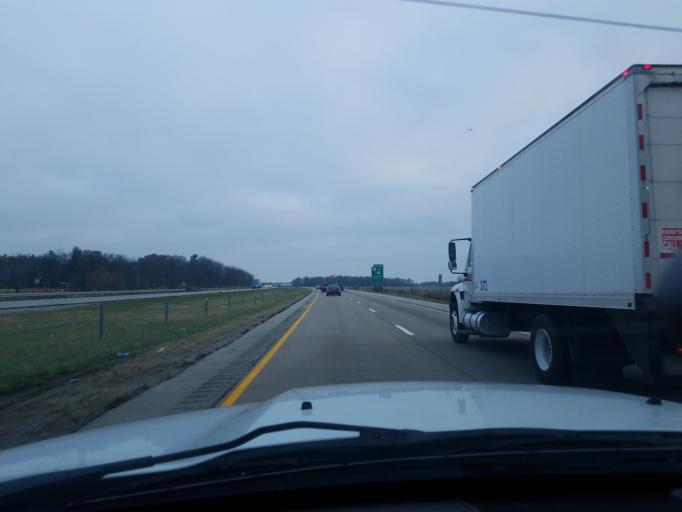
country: US
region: Indiana
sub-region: Delaware County
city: Daleville
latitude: 40.0921
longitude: -85.5710
